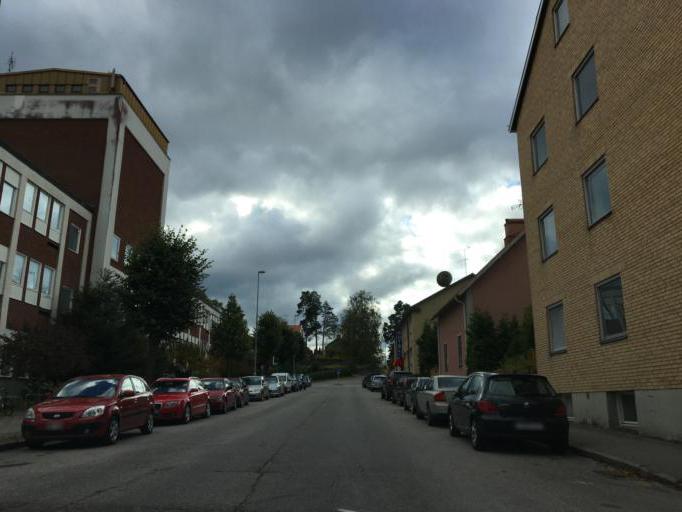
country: SE
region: Soedermanland
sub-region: Katrineholms Kommun
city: Katrineholm
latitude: 58.9929
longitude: 16.2010
